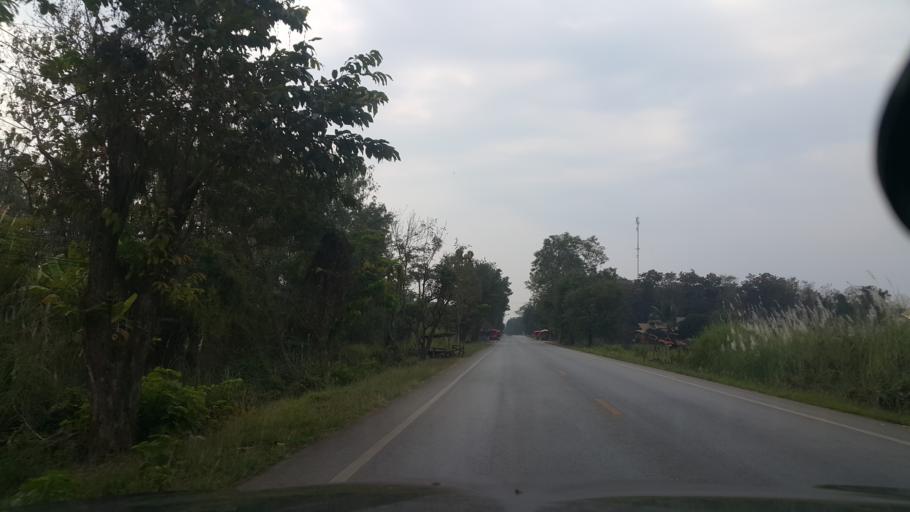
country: TH
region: Sukhothai
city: Si Samrong
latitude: 17.1021
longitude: 99.8869
